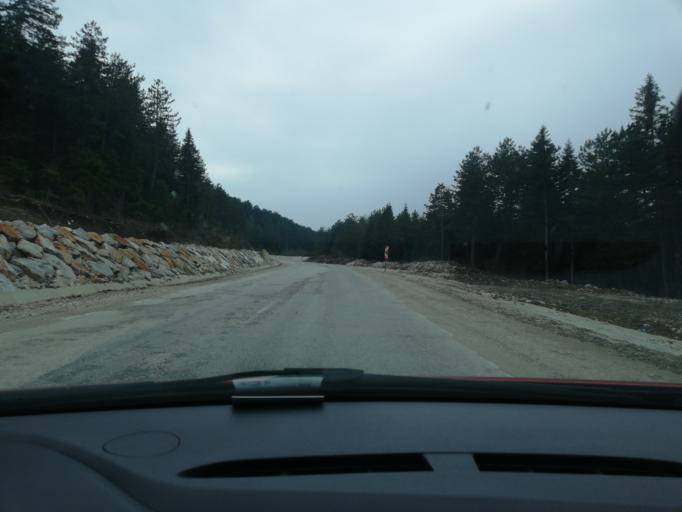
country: TR
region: Kastamonu
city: Pinarbasi
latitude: 41.5635
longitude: 33.0894
